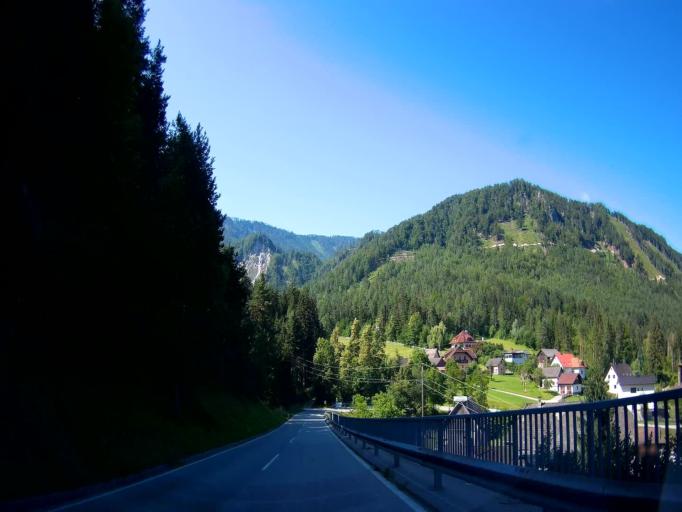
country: AT
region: Carinthia
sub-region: Politischer Bezirk Klagenfurt Land
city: Ebenthal
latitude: 46.5365
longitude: 14.4014
